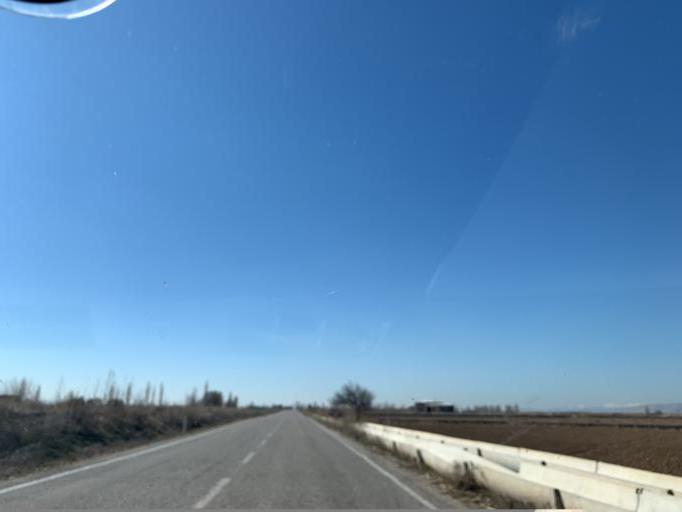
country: TR
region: Konya
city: Cumra
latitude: 37.6171
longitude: 32.7989
